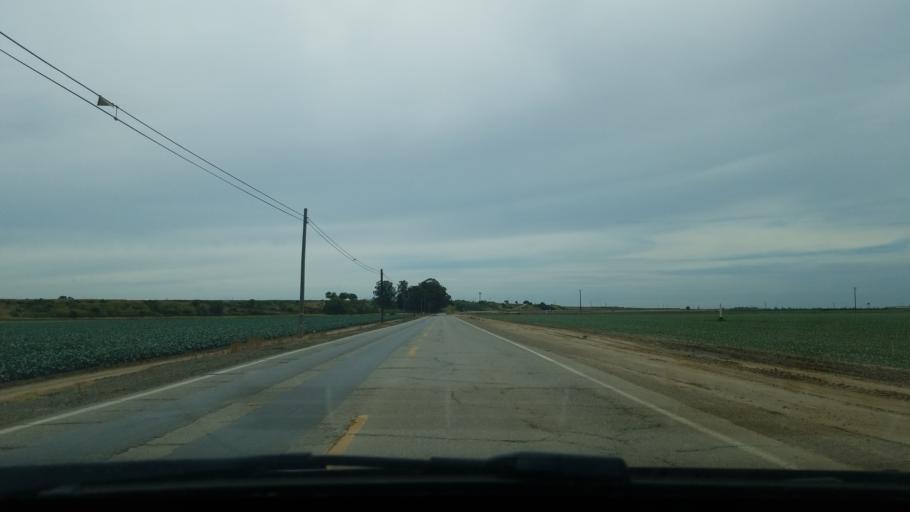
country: US
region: California
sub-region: Santa Barbara County
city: Orcutt
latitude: 34.9085
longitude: -120.3349
